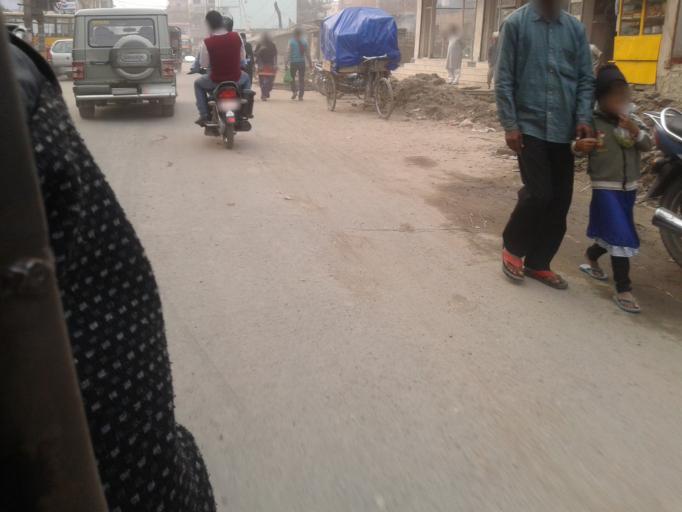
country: IN
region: Bihar
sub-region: Muzaffarpur
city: Muzaffarpur
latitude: 26.1072
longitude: 85.3903
